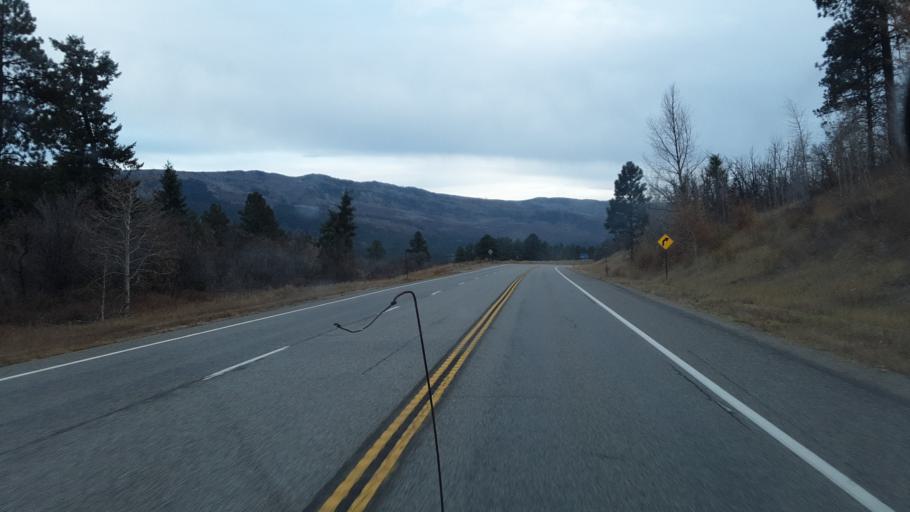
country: US
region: Colorado
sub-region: La Plata County
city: Durango
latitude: 37.5075
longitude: -107.8182
